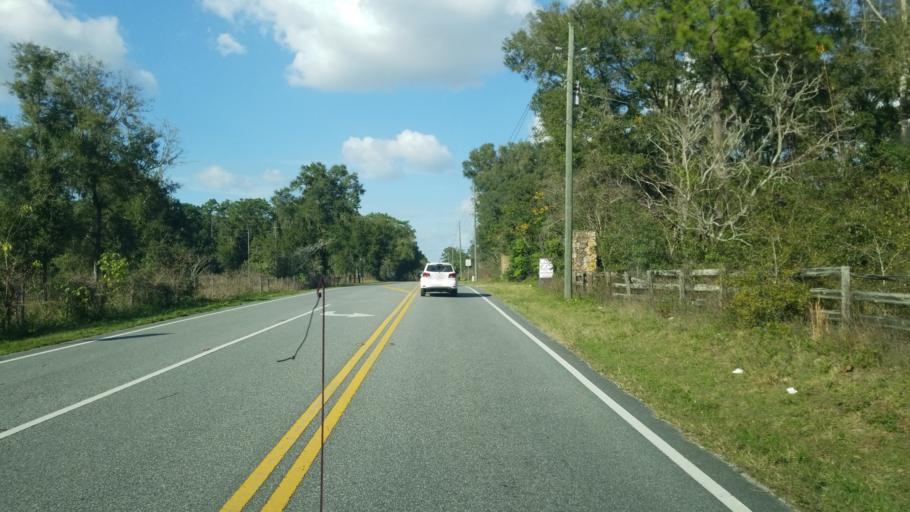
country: US
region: Florida
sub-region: Marion County
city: Ocala
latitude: 29.1569
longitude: -82.2519
